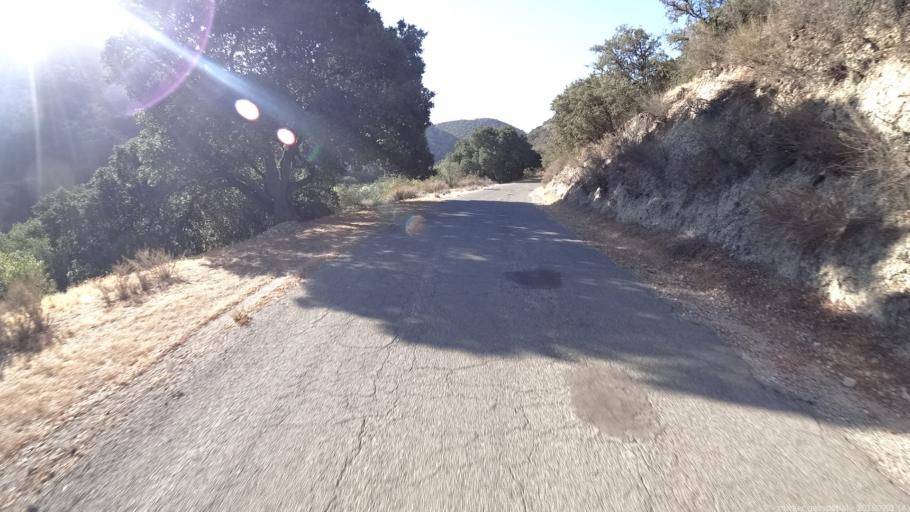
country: US
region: California
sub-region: Monterey County
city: Greenfield
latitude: 36.2236
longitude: -121.2794
